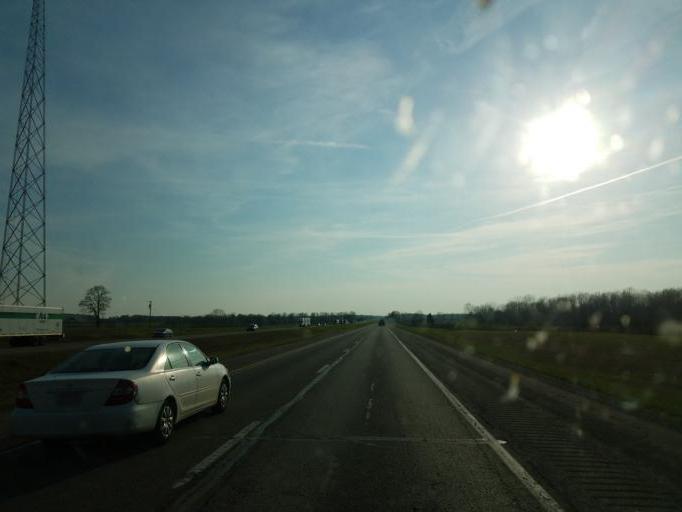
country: US
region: Ohio
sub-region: Warren County
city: Waynesville
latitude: 39.4552
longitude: -84.0036
